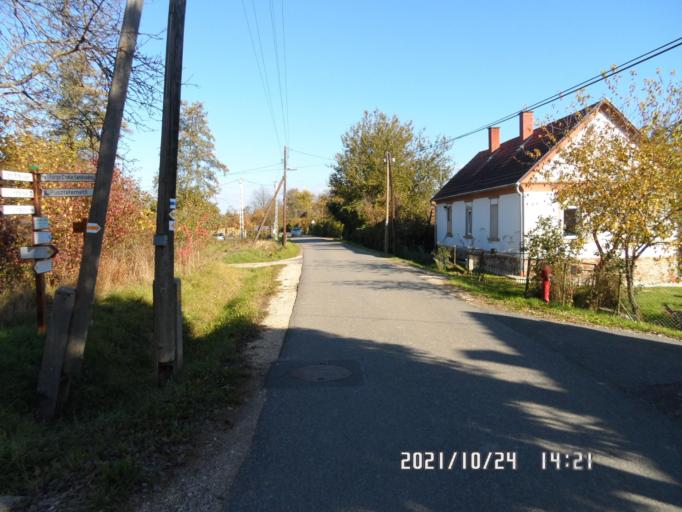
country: SI
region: Hodos-Hodos
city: Hodos
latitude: 46.7844
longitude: 16.3304
